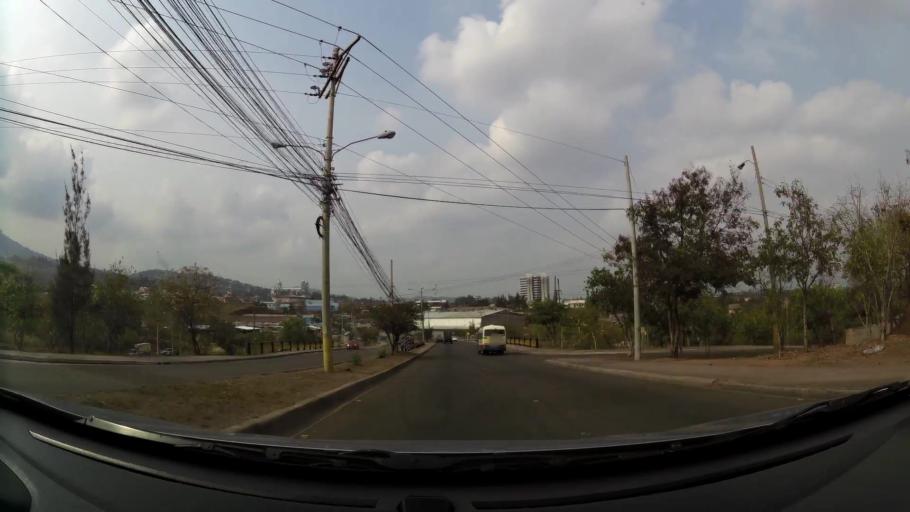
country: HN
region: Francisco Morazan
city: Santa Lucia
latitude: 14.0910
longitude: -87.1578
